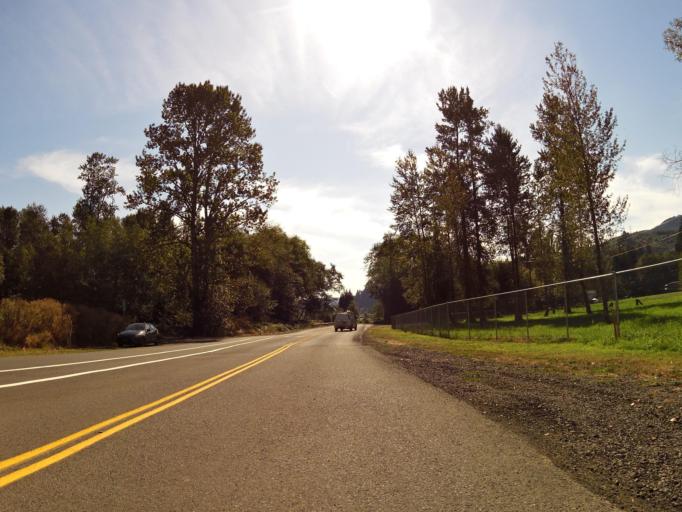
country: US
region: Washington
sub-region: Wahkiakum County
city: Cathlamet
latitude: 46.1363
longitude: -123.3772
